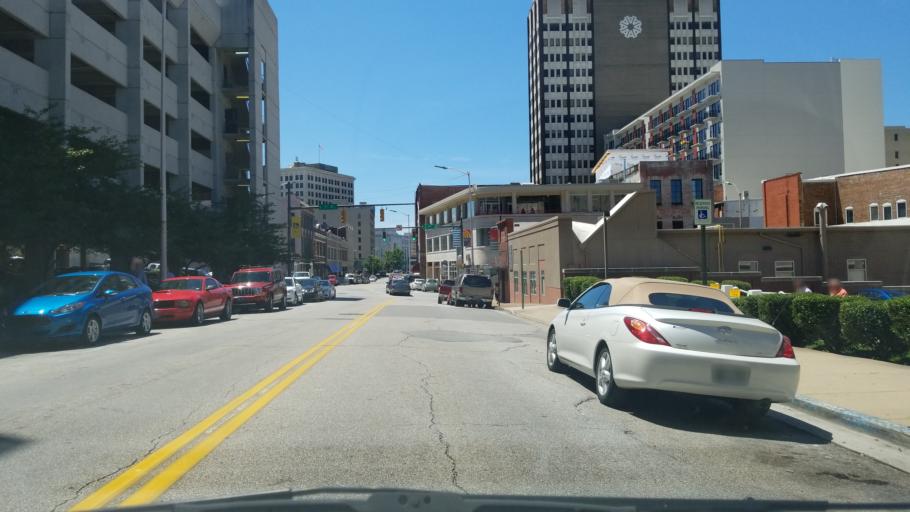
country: US
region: Tennessee
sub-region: Hamilton County
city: Chattanooga
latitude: 35.0490
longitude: -85.3085
